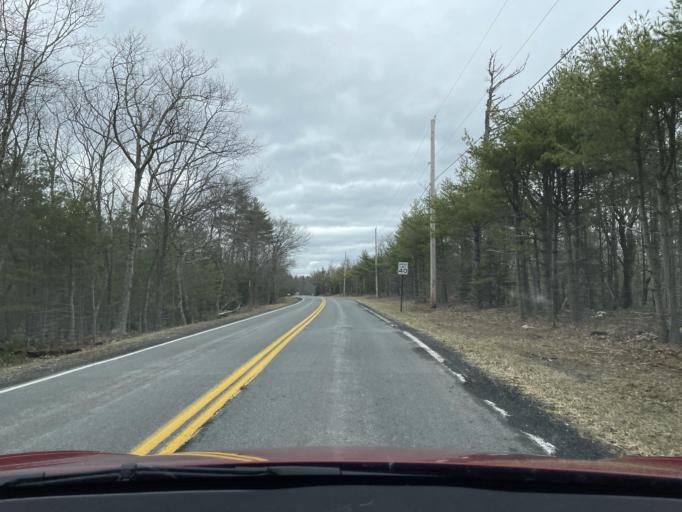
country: US
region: New York
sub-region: Ulster County
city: Zena
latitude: 42.0772
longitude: -74.0676
